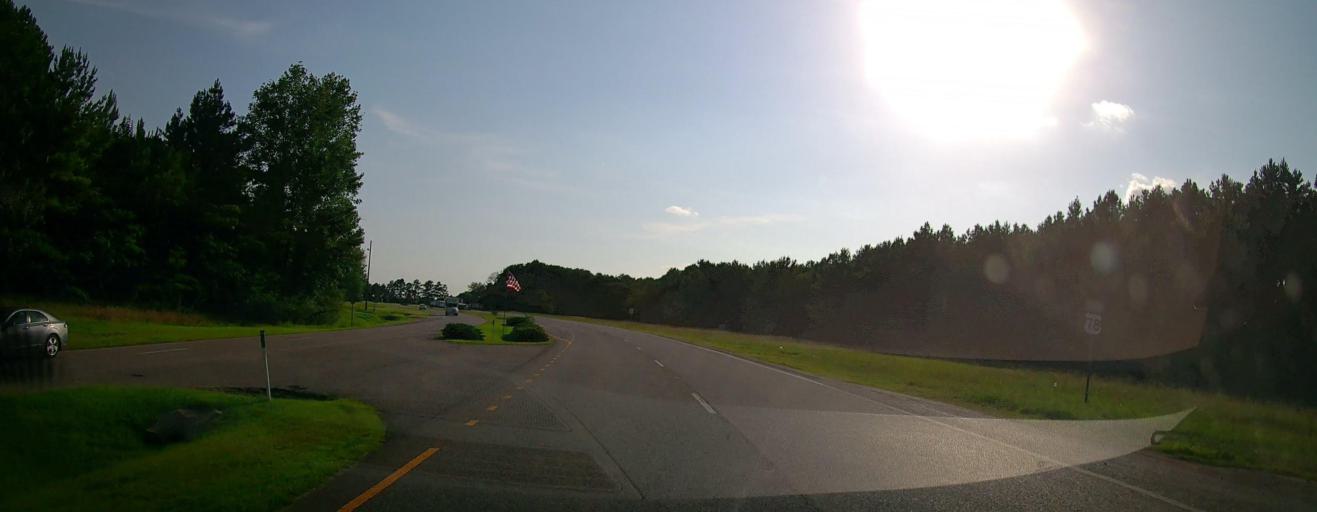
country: US
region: Alabama
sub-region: Jefferson County
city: Irondale
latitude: 33.5465
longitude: -86.6822
